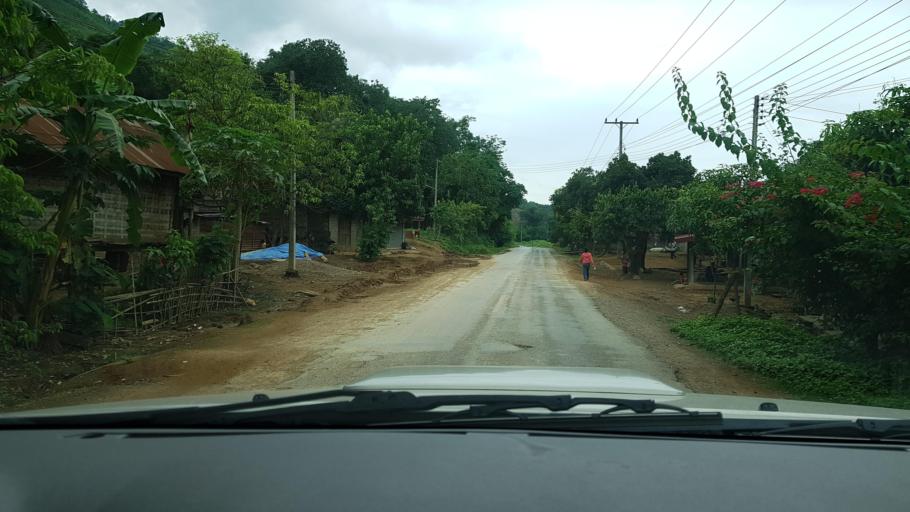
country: LA
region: Loungnamtha
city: Muang Nale
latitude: 20.2184
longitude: 101.5464
